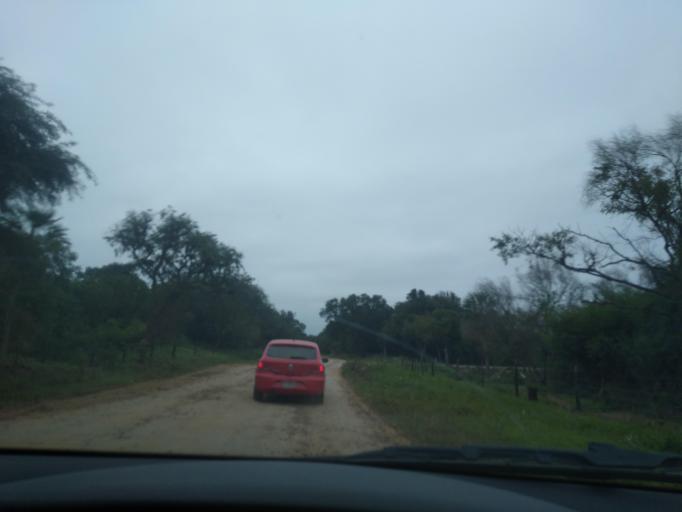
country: AR
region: Chaco
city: Colonia Benitez
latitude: -27.3443
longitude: -58.9701
